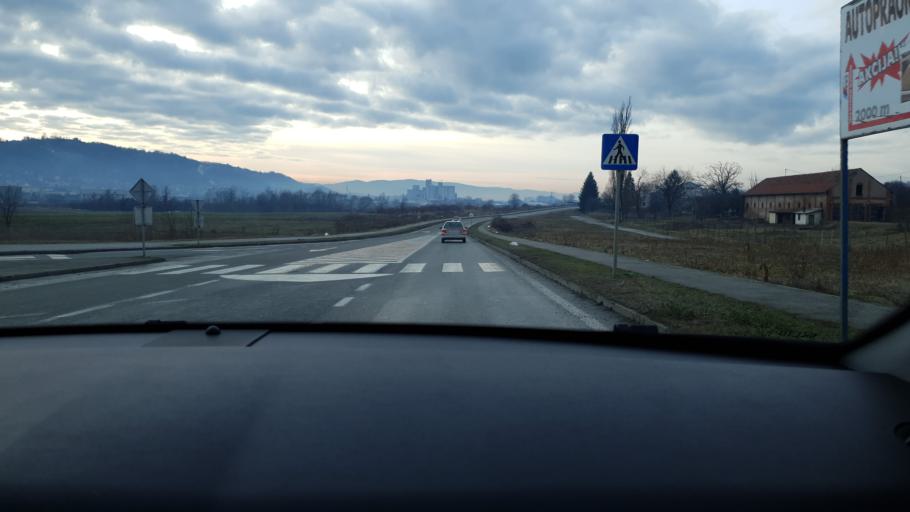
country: HR
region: Pozesko-Slavonska
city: Vidovci
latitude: 45.3419
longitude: 17.7077
